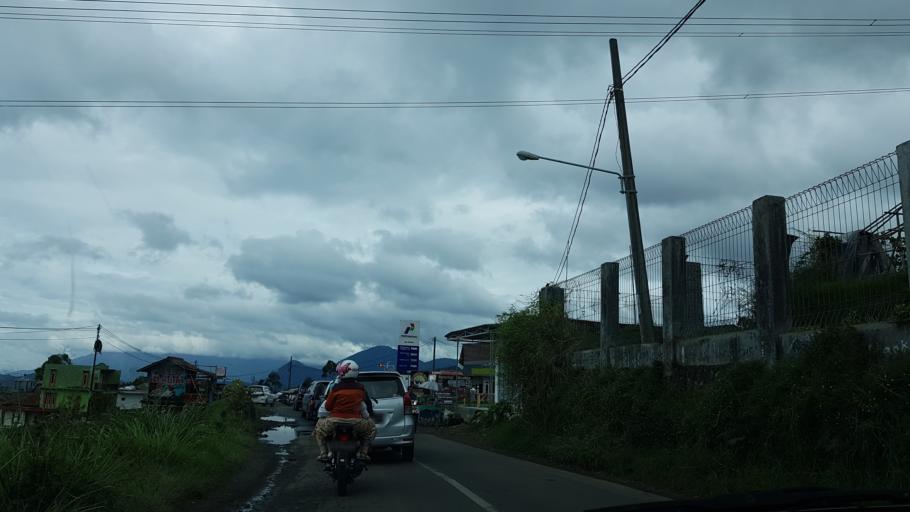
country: ID
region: West Java
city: Banjar
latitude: -7.1221
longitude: 107.4271
